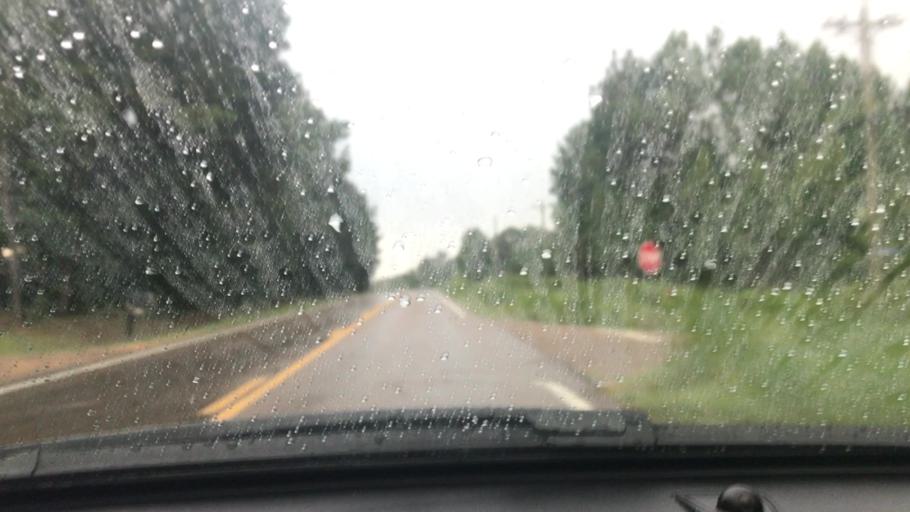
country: US
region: Mississippi
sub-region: Pike County
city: Summit
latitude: 31.3062
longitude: -90.5168
